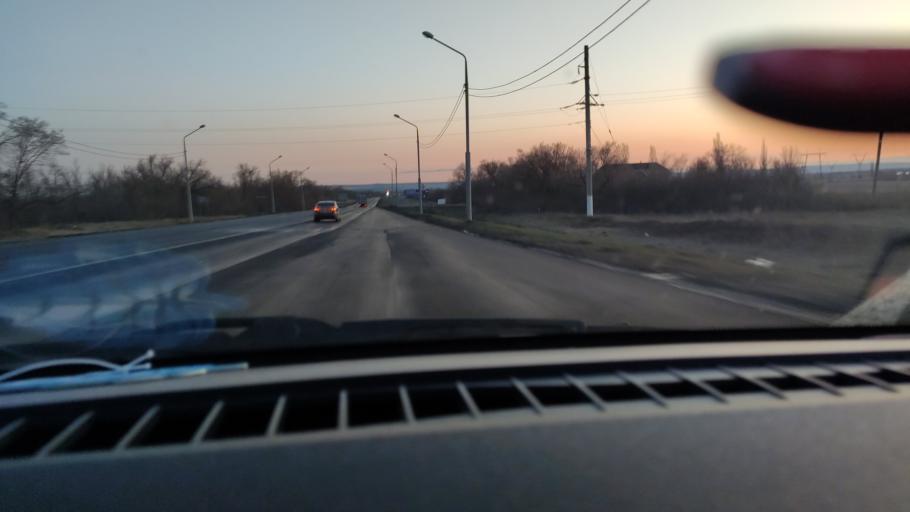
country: RU
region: Saratov
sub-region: Saratovskiy Rayon
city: Saratov
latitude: 51.6737
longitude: 46.0007
